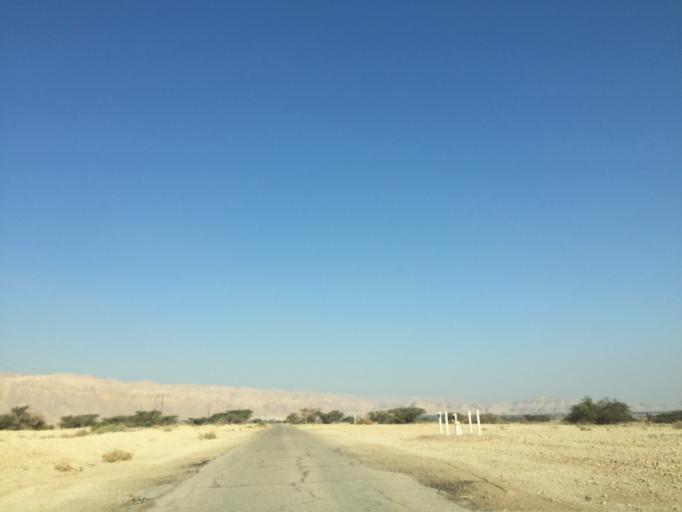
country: JO
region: Ma'an
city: Al Quwayrah
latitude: 29.8375
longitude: 35.0313
